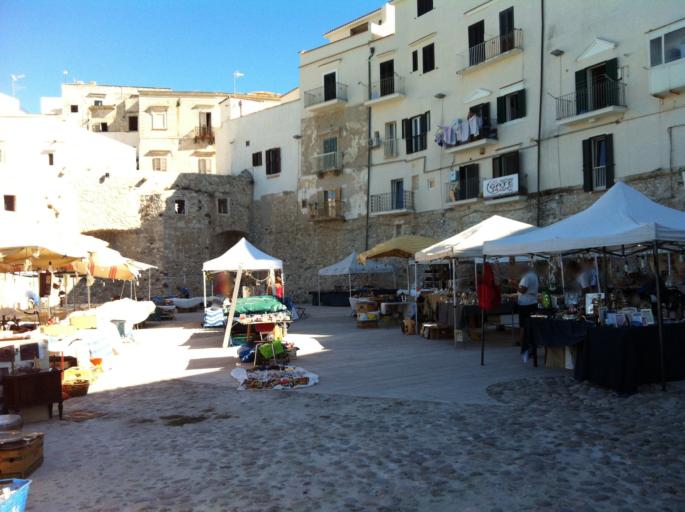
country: IT
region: Apulia
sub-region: Provincia di Foggia
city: Vieste
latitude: 41.8837
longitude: 16.1812
